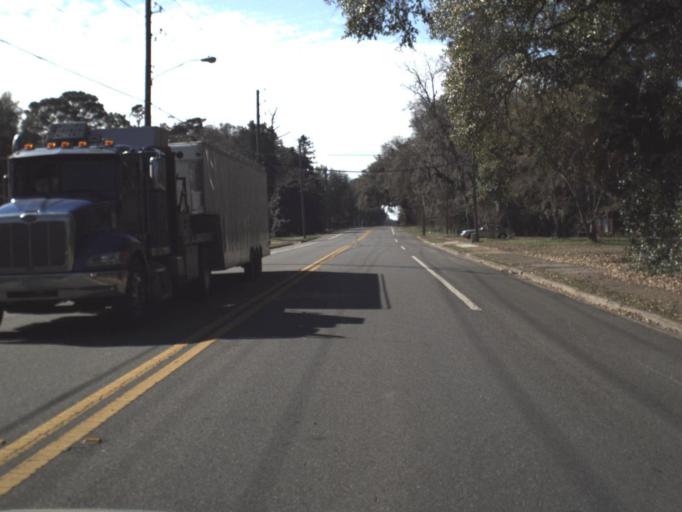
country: US
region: Florida
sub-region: Jackson County
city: Malone
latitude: 30.8677
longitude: -85.1626
